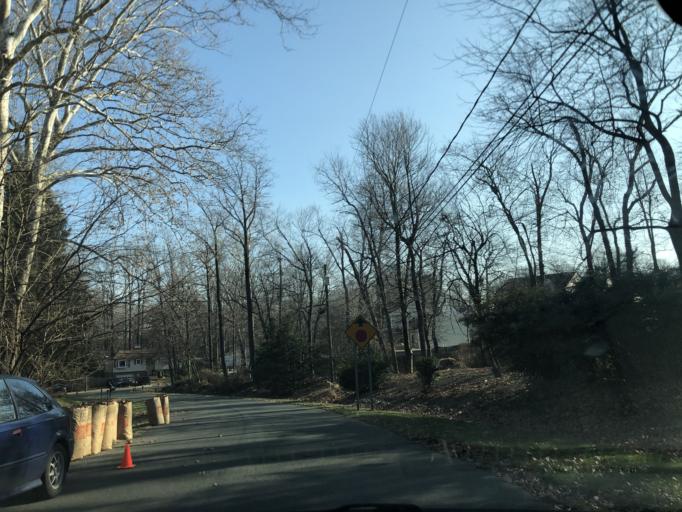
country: US
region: Maryland
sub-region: Montgomery County
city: Burtonsville
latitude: 39.0992
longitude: -76.9386
